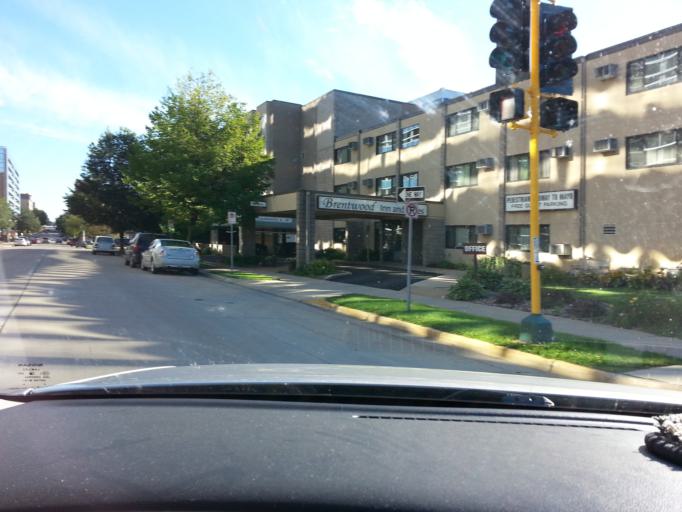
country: US
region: Minnesota
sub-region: Olmsted County
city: Rochester
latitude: 44.0253
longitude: -92.4682
